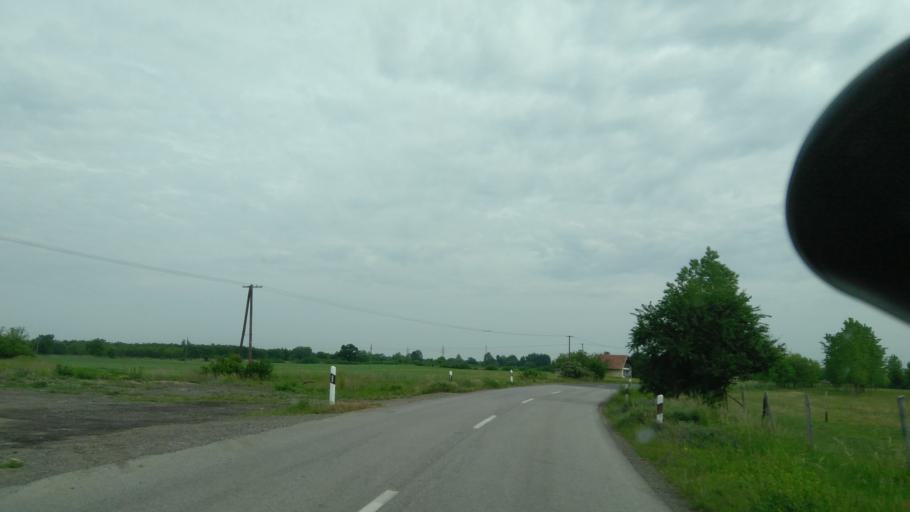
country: HU
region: Bekes
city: Szeghalom
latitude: 46.9987
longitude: 21.1741
